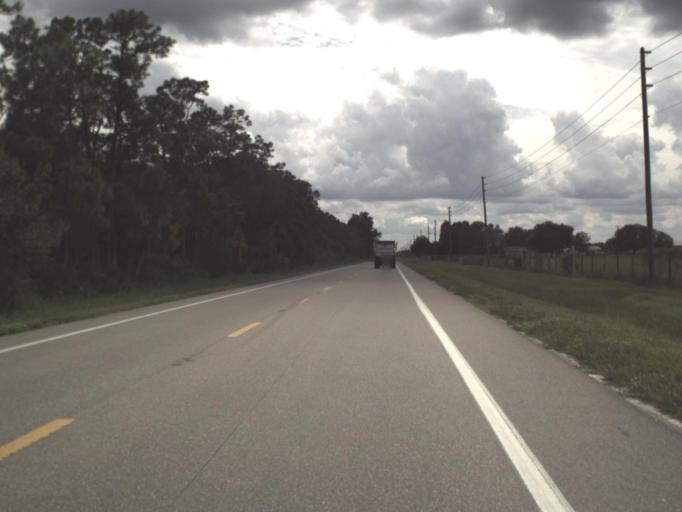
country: US
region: Florida
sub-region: DeSoto County
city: Nocatee
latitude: 27.0023
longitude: -81.7605
